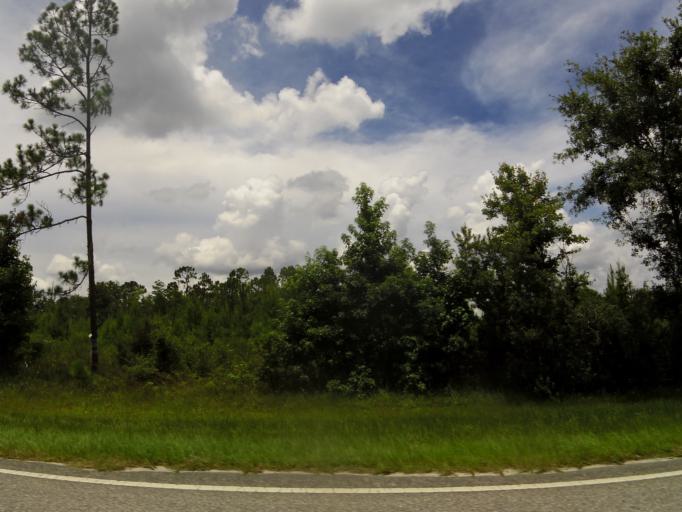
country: US
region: Florida
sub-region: Flagler County
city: Palm Coast
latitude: 29.6562
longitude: -81.3246
